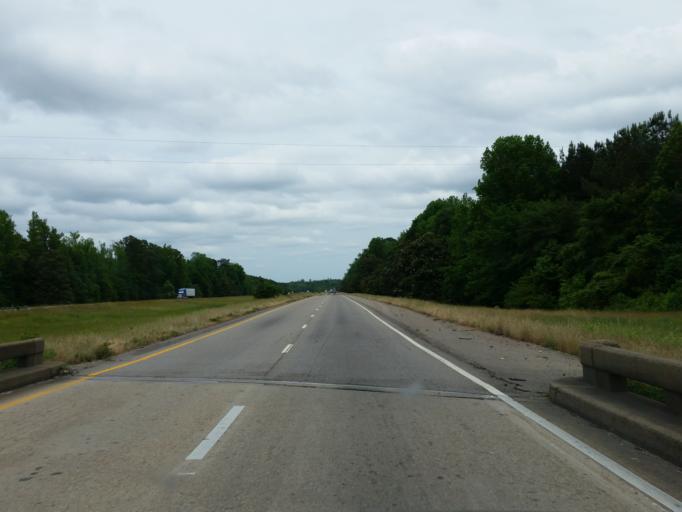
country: US
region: Mississippi
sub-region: Lauderdale County
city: Marion
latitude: 32.4129
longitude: -88.4934
